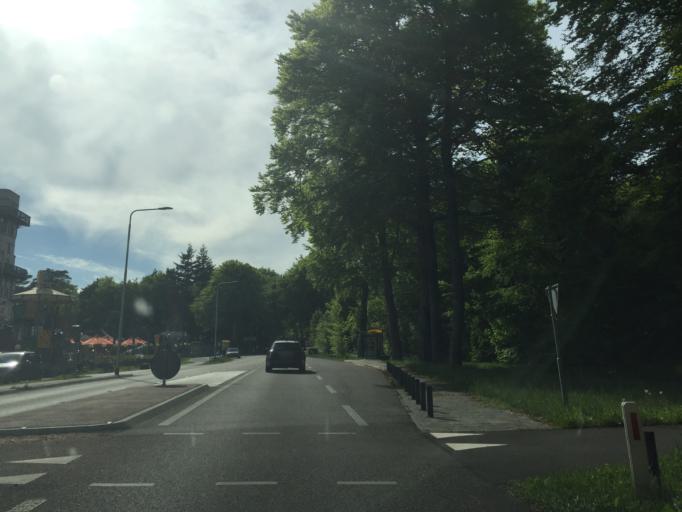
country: NL
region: Gelderland
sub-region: Gemeente Apeldoorn
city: Apeldoorn
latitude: 52.2279
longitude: 5.9177
